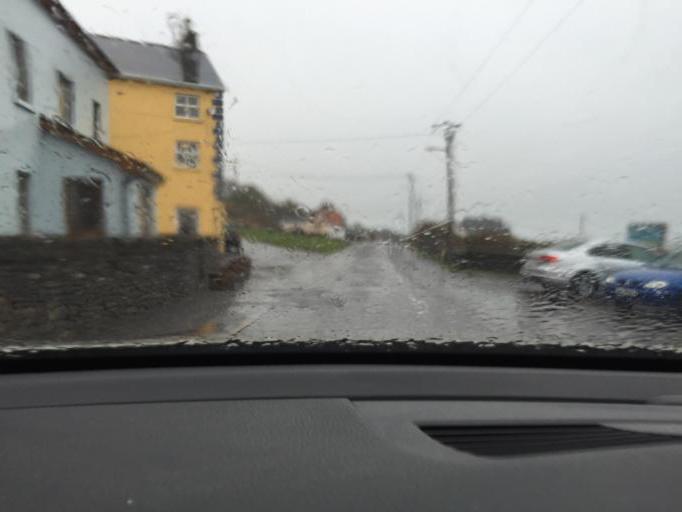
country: IE
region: Munster
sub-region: Ciarrai
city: Dingle
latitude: 52.1329
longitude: -10.3604
